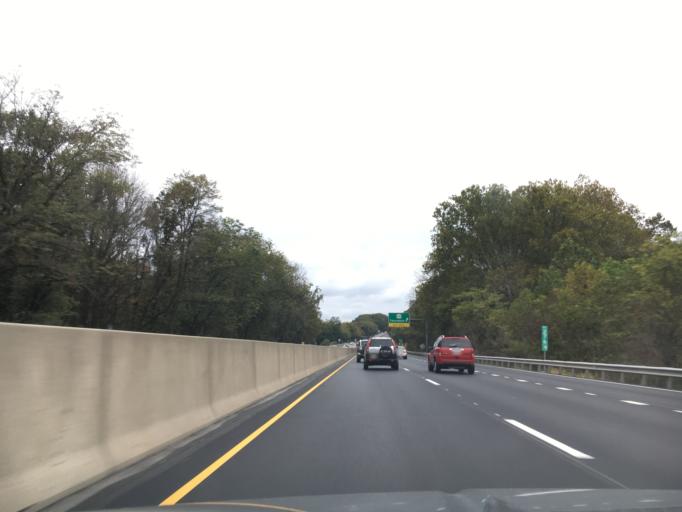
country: US
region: Pennsylvania
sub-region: Chester County
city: Thorndale
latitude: 40.0088
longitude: -75.7414
